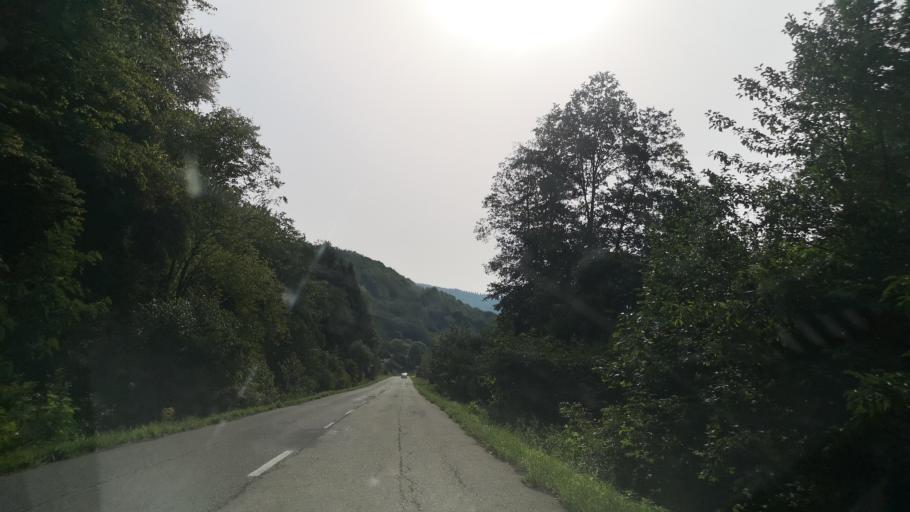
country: SK
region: Banskobystricky
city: Poltar
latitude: 48.5785
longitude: 19.8161
